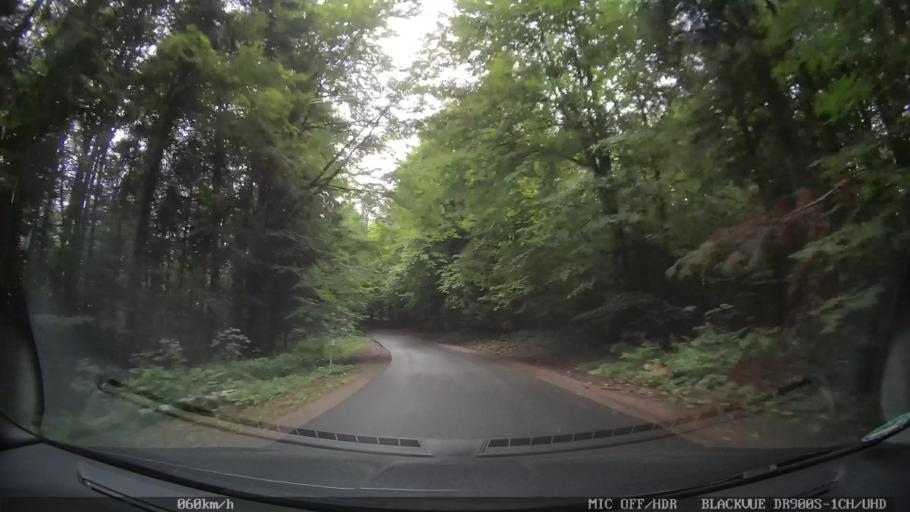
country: HR
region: Licko-Senjska
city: Jezerce
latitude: 44.9341
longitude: 15.5498
